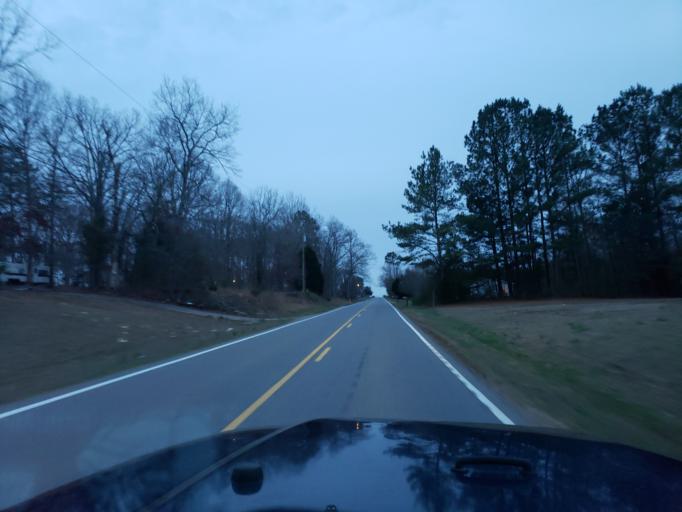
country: US
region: North Carolina
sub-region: Cleveland County
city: White Plains
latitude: 35.2213
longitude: -81.4569
